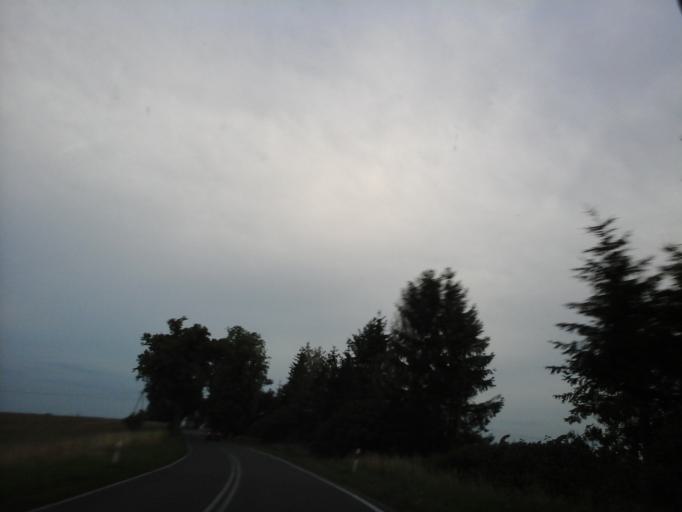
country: PL
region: West Pomeranian Voivodeship
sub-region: Powiat stargardzki
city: Stargard Szczecinski
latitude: 53.3592
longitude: 15.0614
